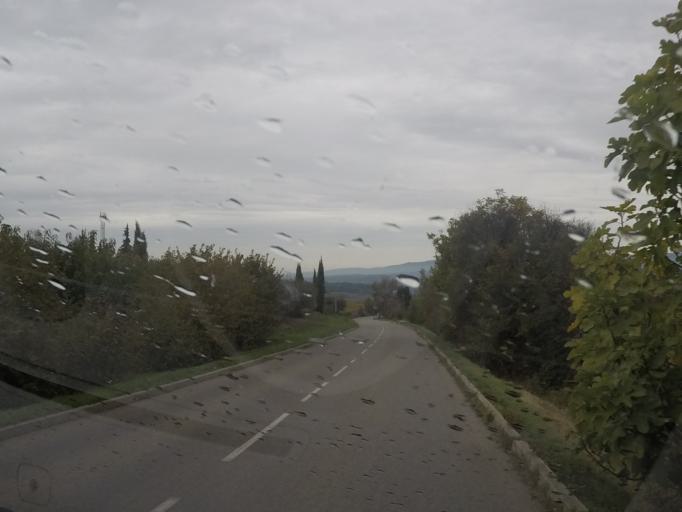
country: FR
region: Provence-Alpes-Cote d'Azur
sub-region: Departement du Vaucluse
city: Bonnieux
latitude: 43.8263
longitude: 5.3026
